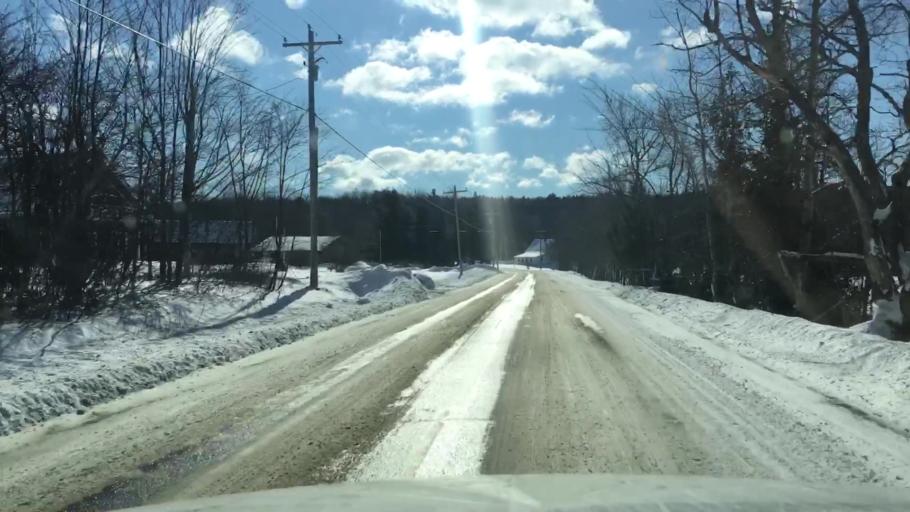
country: US
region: Maine
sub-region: Washington County
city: Calais
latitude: 45.0648
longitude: -67.4720
